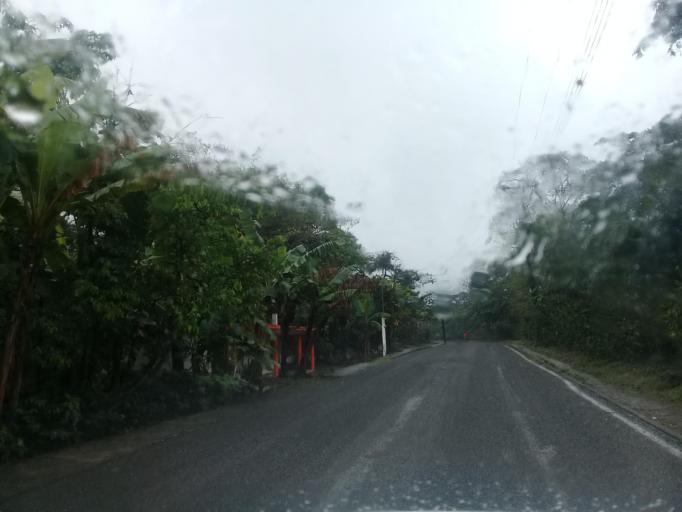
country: MX
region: Veracruz
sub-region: Amatlan de los Reyes
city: Centro de Readaptacion Social
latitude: 18.8005
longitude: -96.9452
